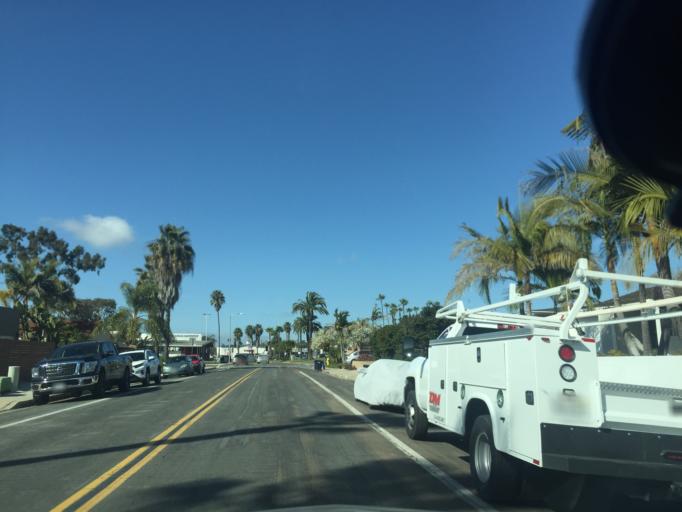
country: US
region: California
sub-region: San Diego County
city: San Diego
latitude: 32.7926
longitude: -117.1933
